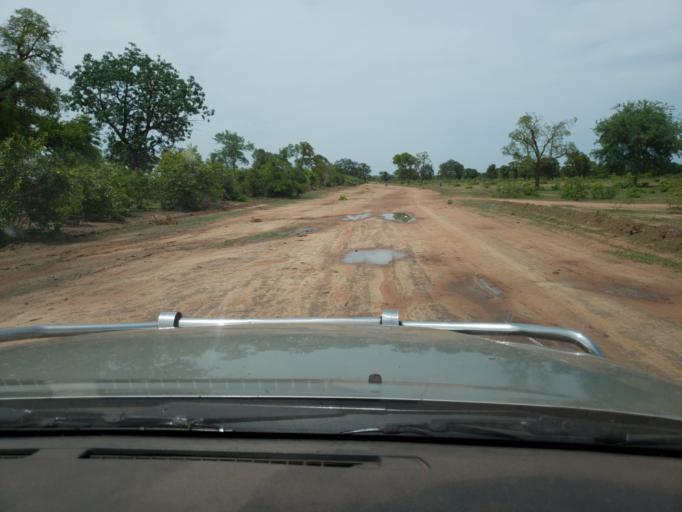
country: ML
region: Koulikoro
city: Kolokani
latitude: 13.4920
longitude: -8.2437
